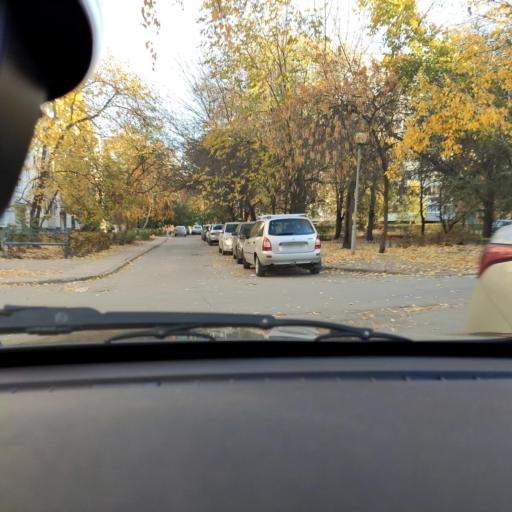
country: RU
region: Samara
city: Tol'yatti
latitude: 53.5346
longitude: 49.3049
